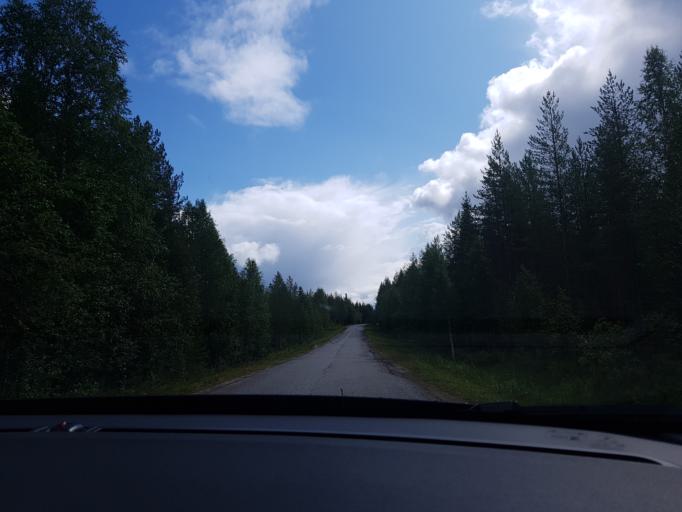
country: FI
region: Kainuu
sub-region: Kehys-Kainuu
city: Kuhmo
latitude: 64.4497
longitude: 29.6861
